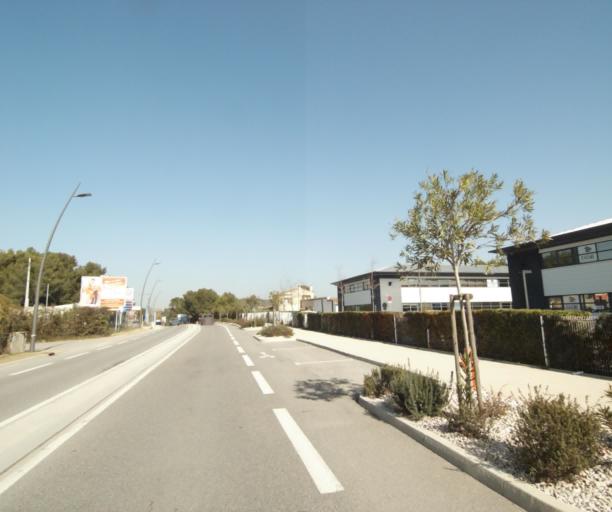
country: FR
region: Provence-Alpes-Cote d'Azur
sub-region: Departement des Bouches-du-Rhone
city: Cabries
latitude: 43.4343
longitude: 5.3969
